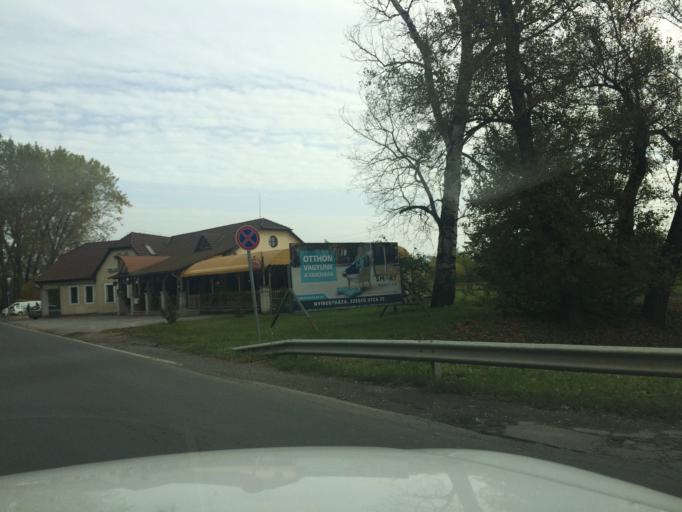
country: HU
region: Szabolcs-Szatmar-Bereg
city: Nyiregyhaza
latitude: 47.9990
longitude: 21.7304
